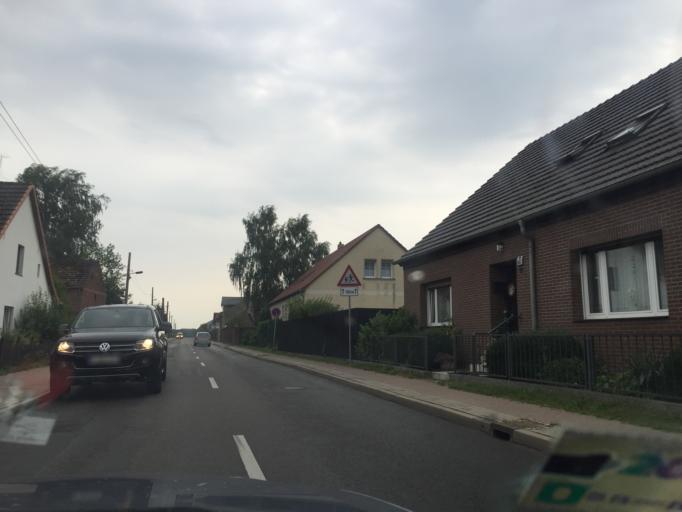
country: DE
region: Brandenburg
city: Wandlitz
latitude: 52.7809
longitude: 13.3887
